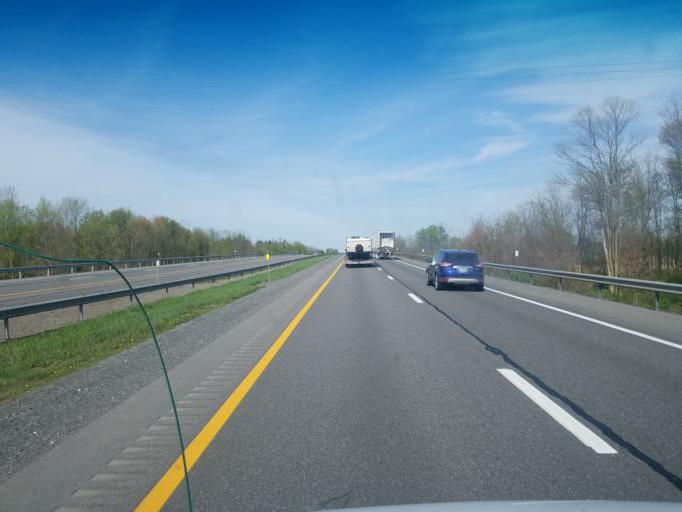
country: US
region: New York
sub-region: Madison County
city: Oneida
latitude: 43.1110
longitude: -75.6625
